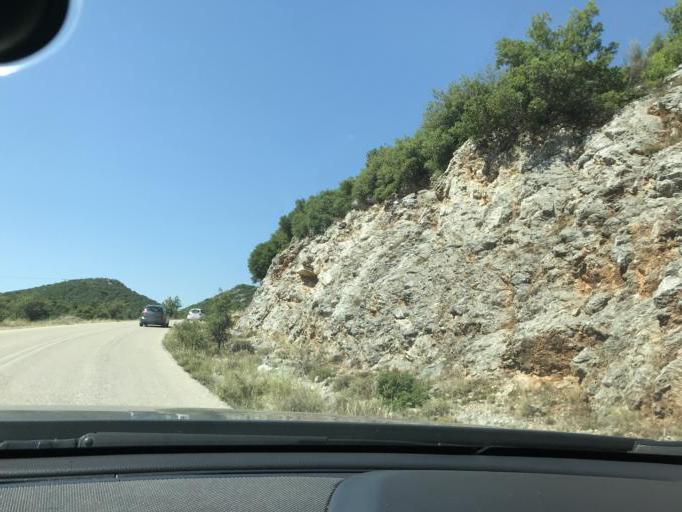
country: GR
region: Central Greece
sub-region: Nomos Voiotias
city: Distomo
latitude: 38.4985
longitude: 22.7005
